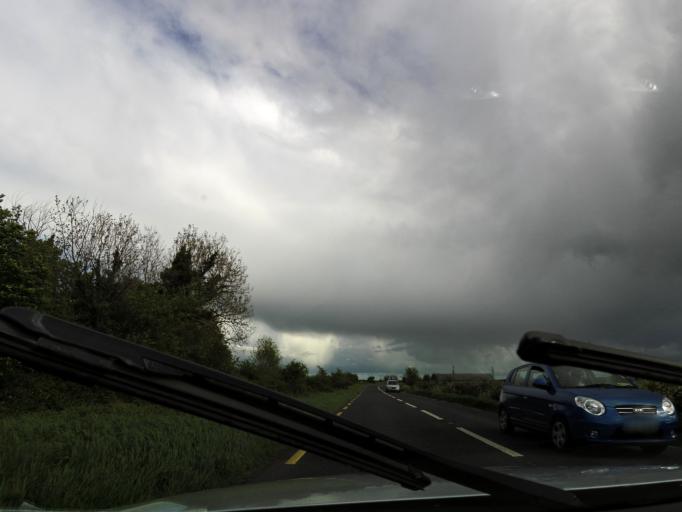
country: IE
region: Munster
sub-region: North Tipperary
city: Templemore
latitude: 52.7340
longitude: -7.8387
